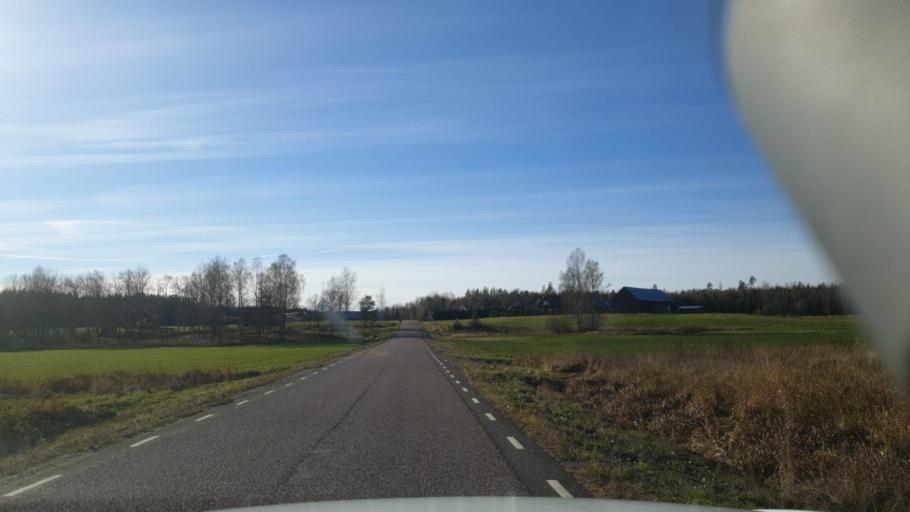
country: SE
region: Vaermland
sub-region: Karlstads Kommun
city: Edsvalla
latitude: 59.4907
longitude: 13.0973
